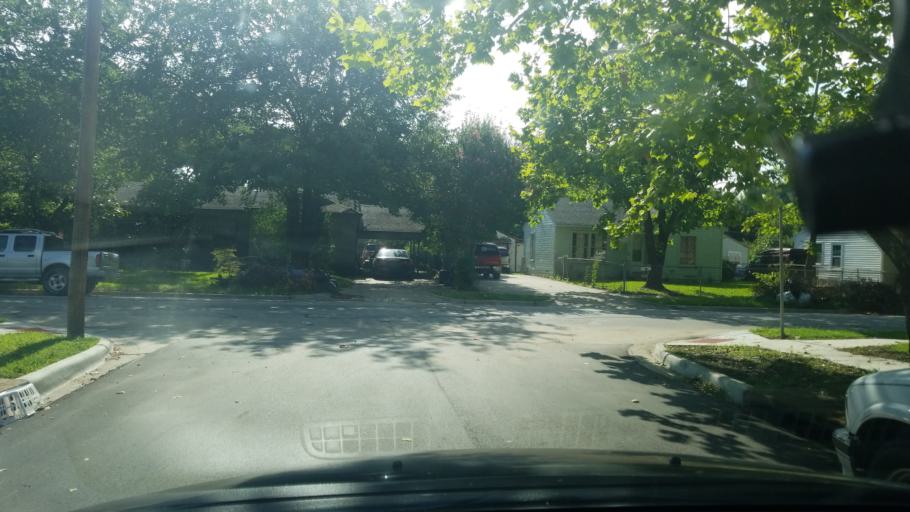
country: US
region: Texas
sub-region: Dallas County
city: Balch Springs
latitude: 32.7414
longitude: -96.6707
